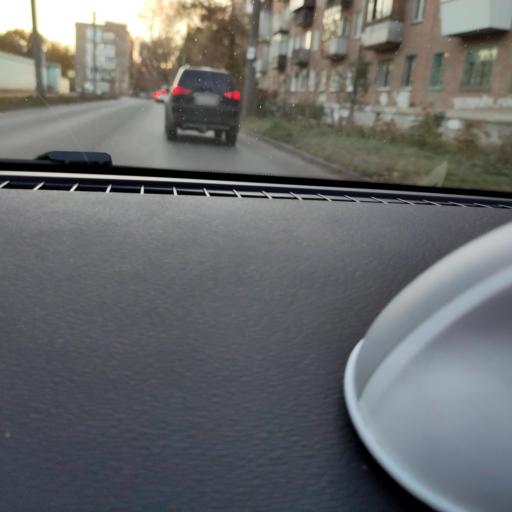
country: RU
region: Samara
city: Samara
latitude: 53.2031
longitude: 50.2315
